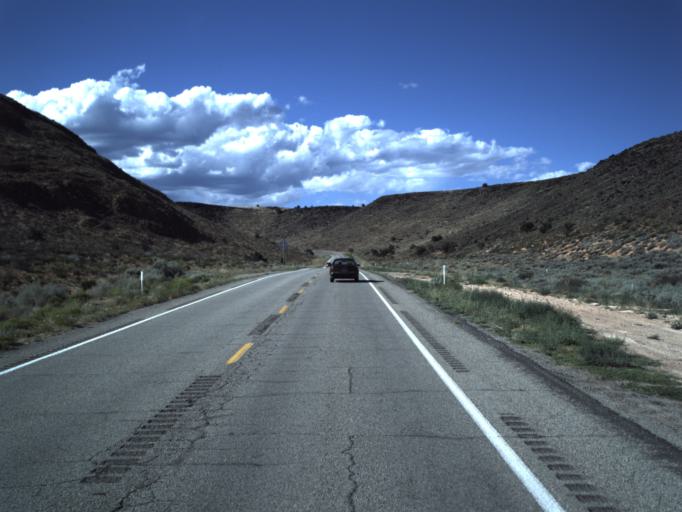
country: US
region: Utah
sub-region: Washington County
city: Toquerville
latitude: 37.2666
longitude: -113.2957
